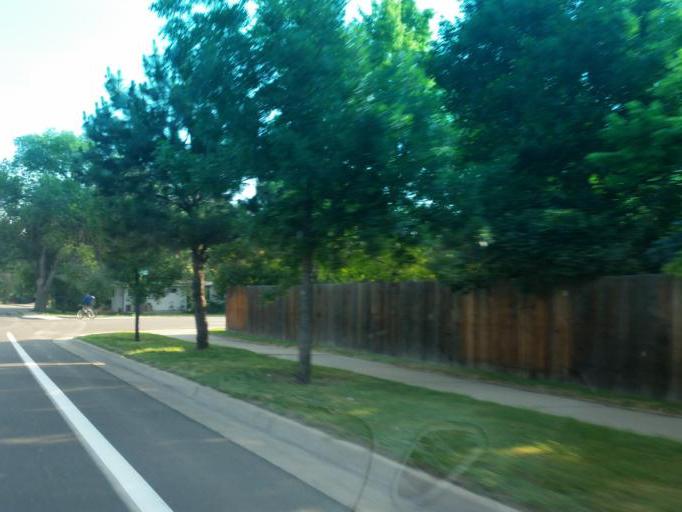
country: US
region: Colorado
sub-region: Larimer County
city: Fort Collins
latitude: 40.5616
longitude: -105.1151
